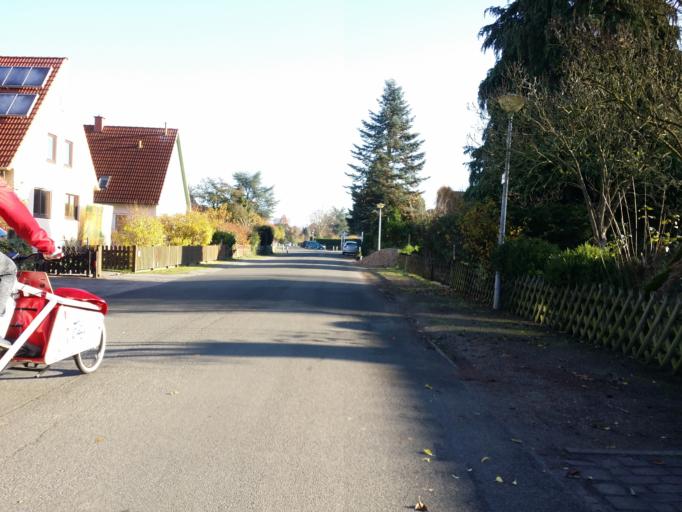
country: DE
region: Lower Saxony
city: Lilienthal
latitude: 53.0729
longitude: 8.9062
